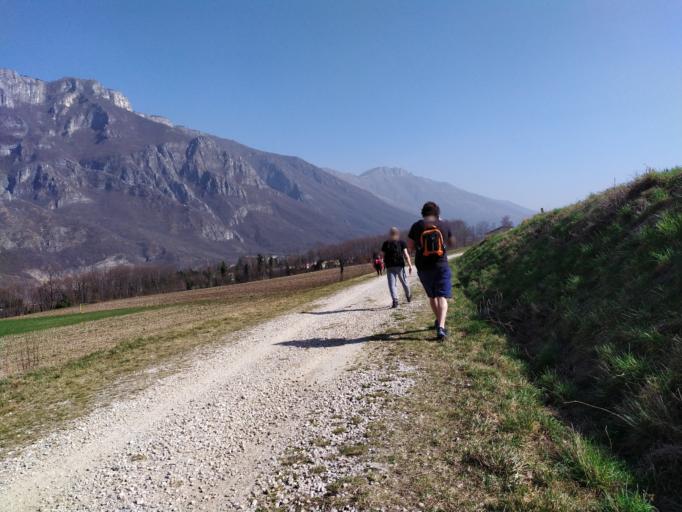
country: IT
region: Veneto
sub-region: Provincia di Vicenza
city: Velo
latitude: 45.7965
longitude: 11.3631
